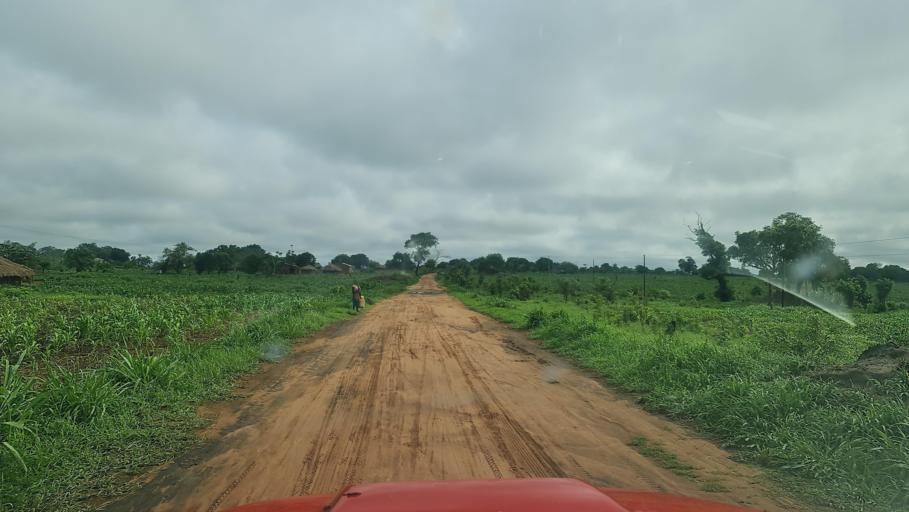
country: MW
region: Southern Region
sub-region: Nsanje District
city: Nsanje
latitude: -17.2075
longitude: 35.6809
